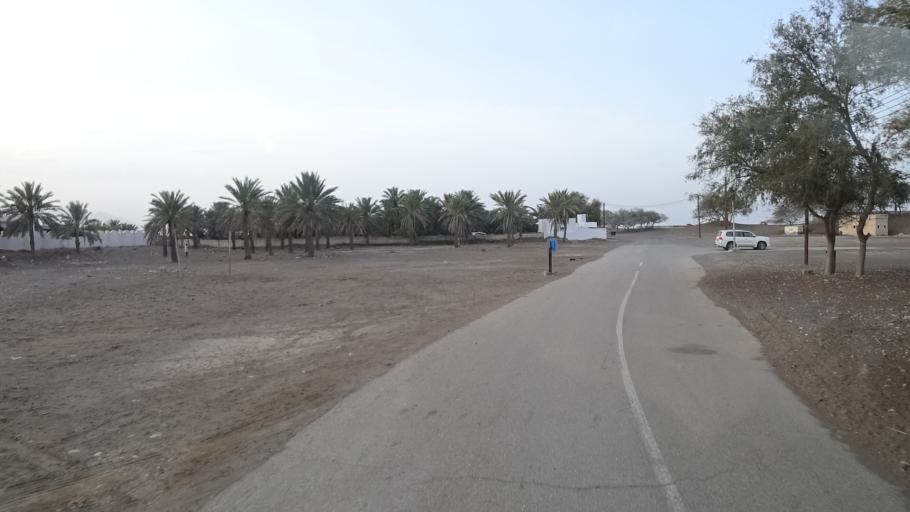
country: OM
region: Muhafazat Masqat
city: Muscat
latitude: 23.2165
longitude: 58.9743
